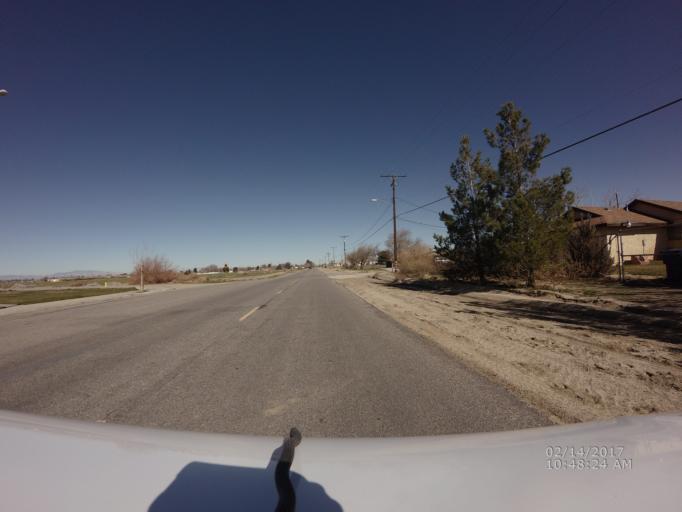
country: US
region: California
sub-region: Los Angeles County
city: Littlerock
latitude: 34.5685
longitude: -117.9521
